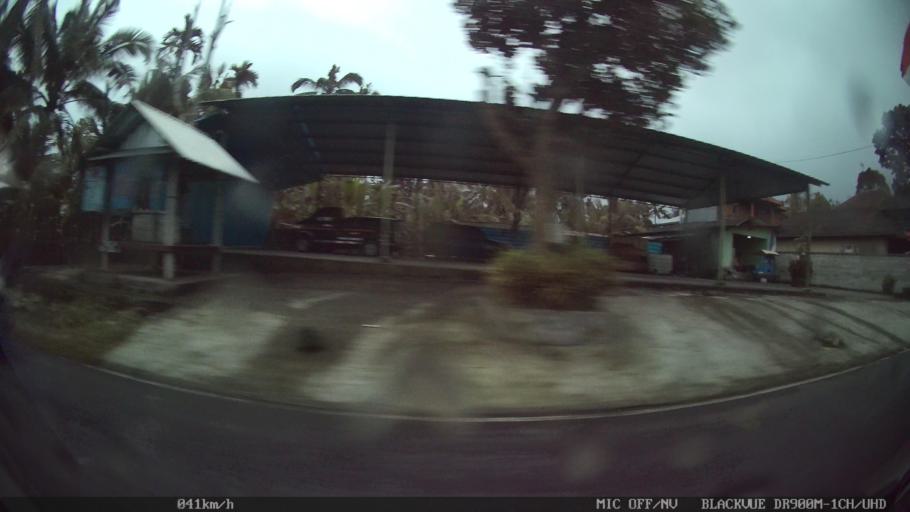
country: ID
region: Bali
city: Banjar Ponggang
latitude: -8.3920
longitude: 115.2569
